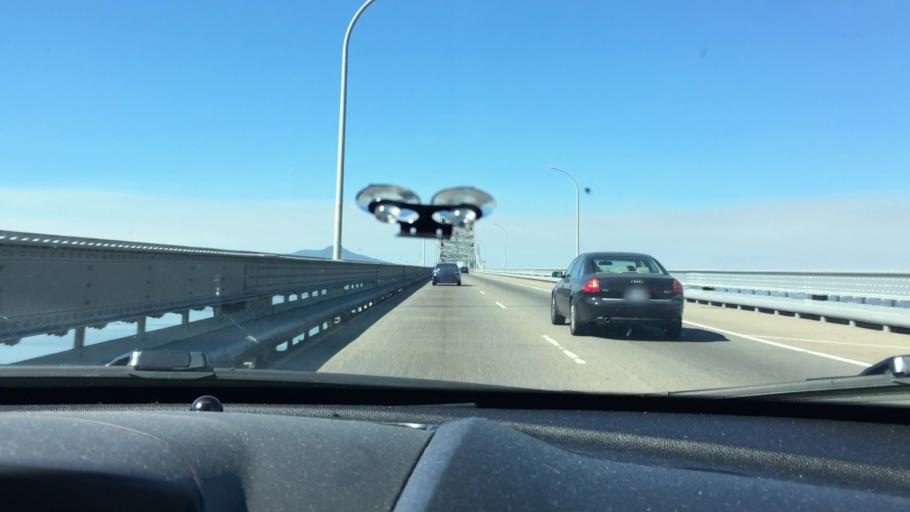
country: US
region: California
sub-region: Contra Costa County
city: North Richmond
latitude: 37.9335
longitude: -122.4206
